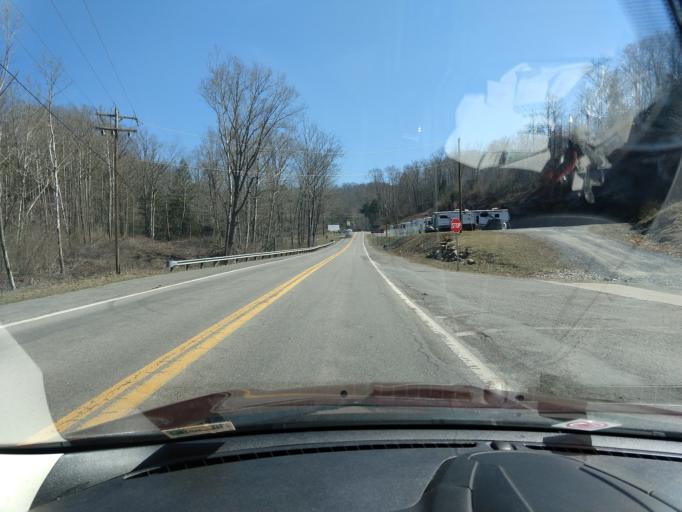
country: US
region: West Virginia
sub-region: Braxton County
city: Sutton
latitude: 38.6891
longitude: -80.6788
